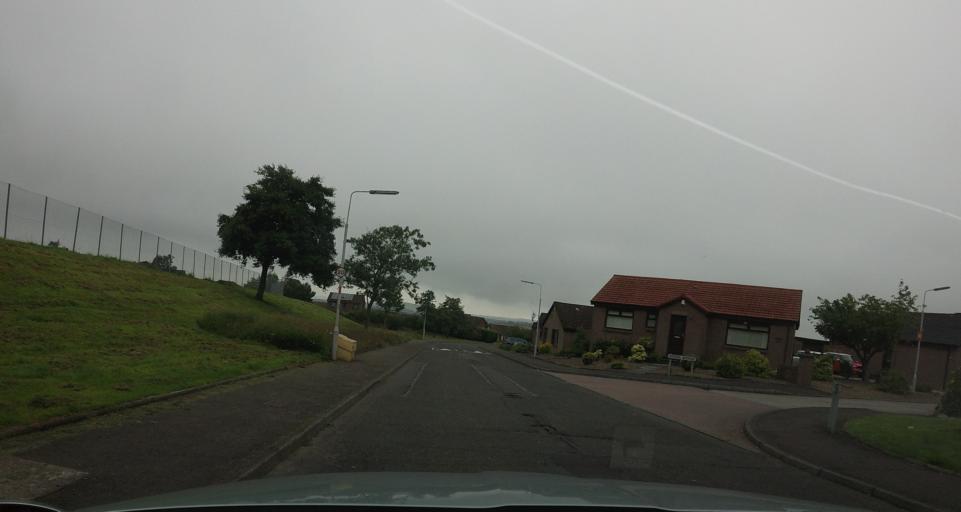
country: GB
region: Scotland
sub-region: Fife
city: Kelty
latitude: 56.1352
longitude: -3.3774
